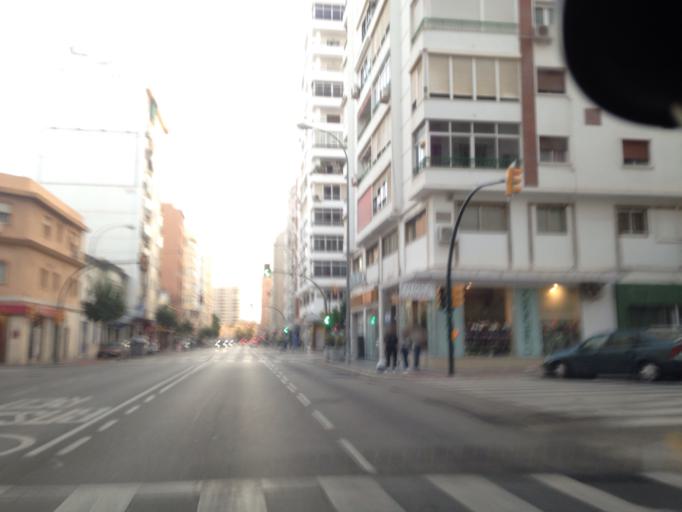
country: ES
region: Andalusia
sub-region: Provincia de Malaga
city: Malaga
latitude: 36.7234
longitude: -4.4357
